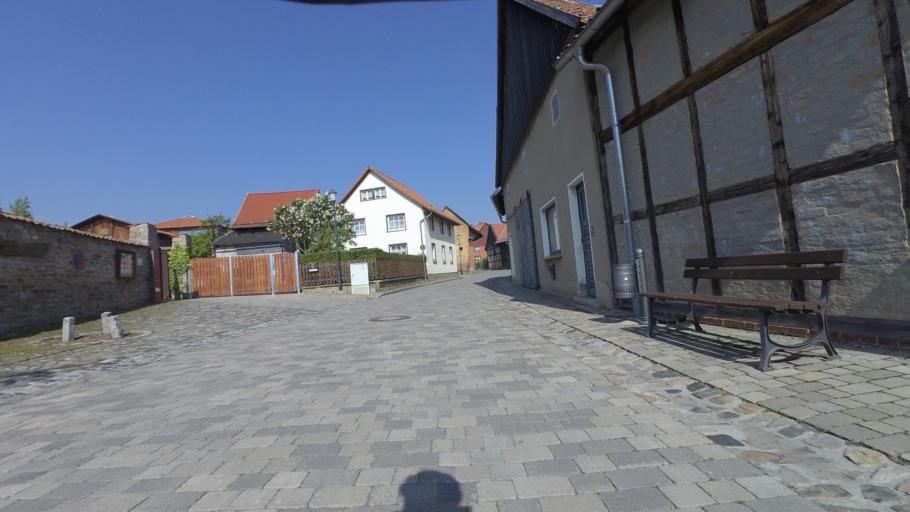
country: DE
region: Saxony-Anhalt
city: Drubeck
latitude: 51.8567
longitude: 10.7159
